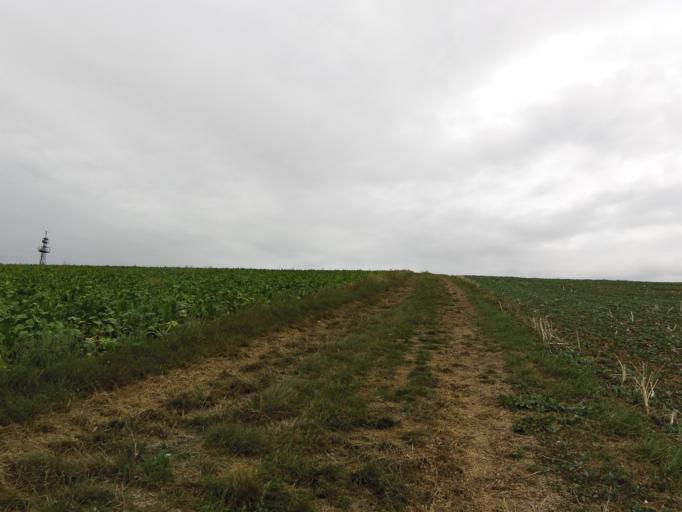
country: DE
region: Bavaria
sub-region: Regierungsbezirk Unterfranken
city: Rimpar
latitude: 49.8383
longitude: 9.9473
